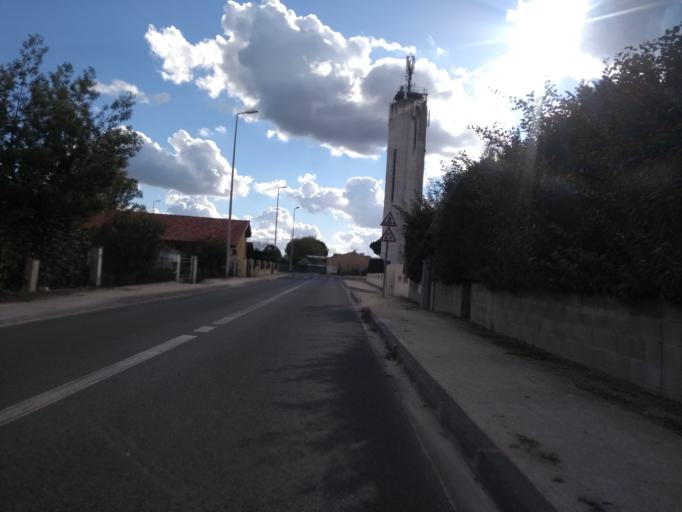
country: FR
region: Aquitaine
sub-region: Departement de la Gironde
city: Cestas
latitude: 44.7419
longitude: -0.6598
